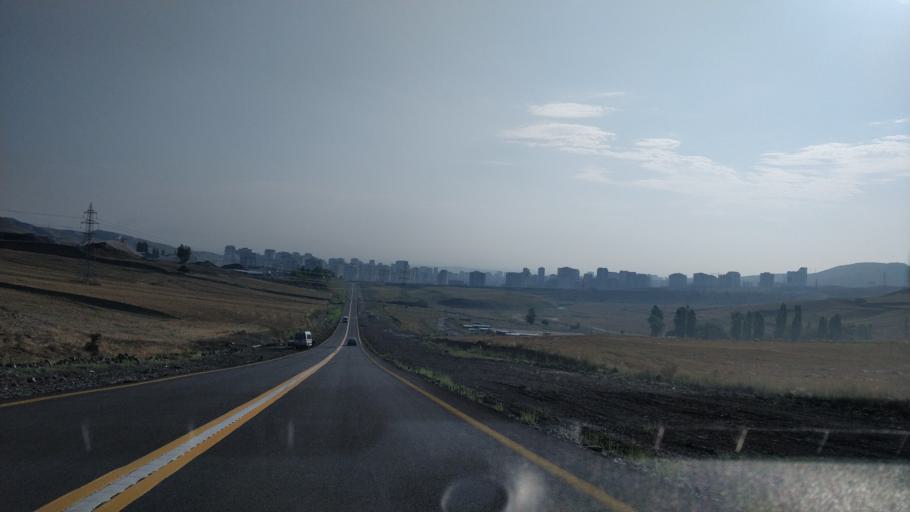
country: TR
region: Ankara
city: Etimesgut
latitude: 39.8783
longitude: 32.6018
